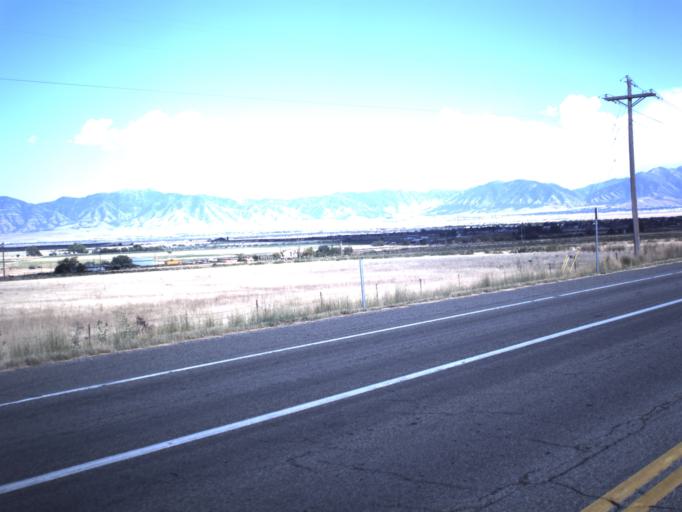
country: US
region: Utah
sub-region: Tooele County
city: Grantsville
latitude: 40.6276
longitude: -112.5103
